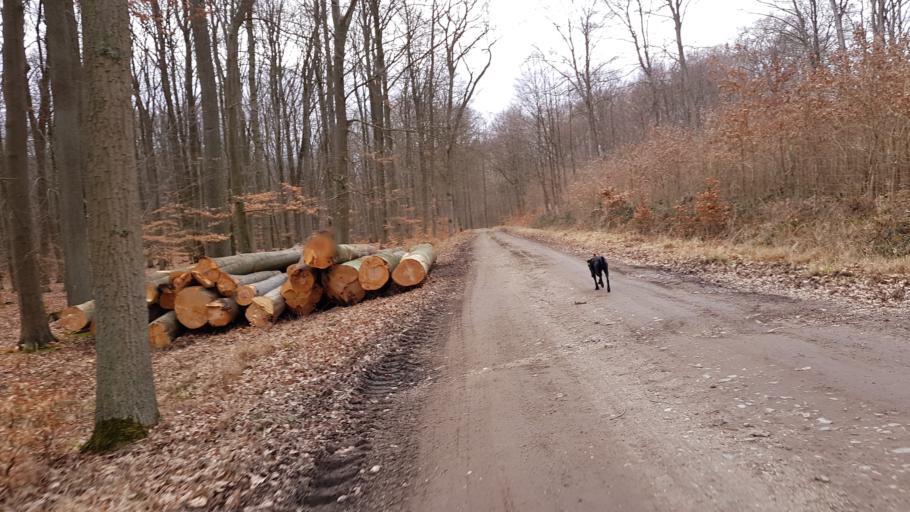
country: PL
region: West Pomeranian Voivodeship
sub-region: Powiat gryfinski
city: Banie
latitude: 53.0877
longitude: 14.7334
